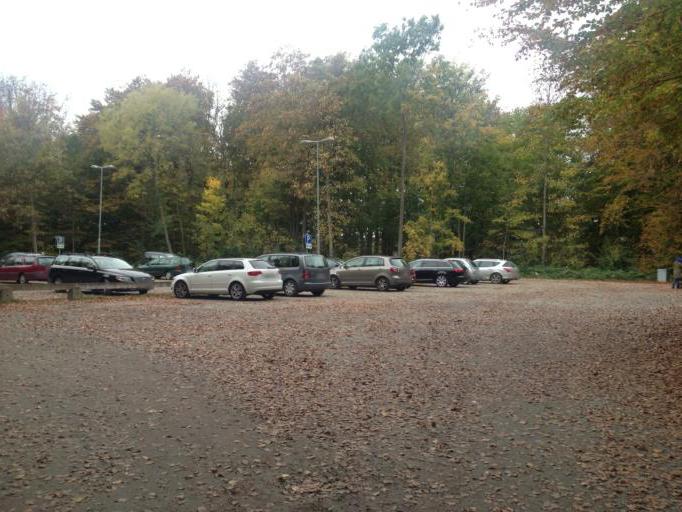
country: SE
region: Skane
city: Bjarred
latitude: 55.7127
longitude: 13.0278
